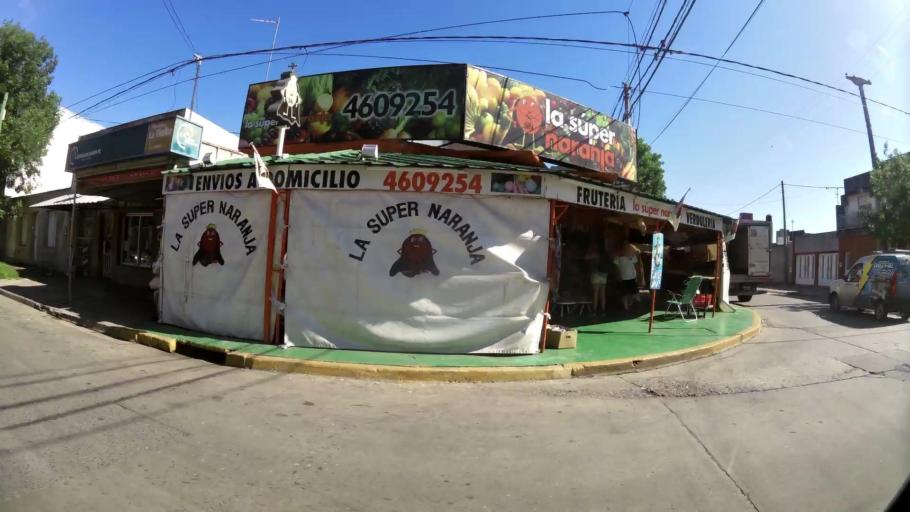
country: AR
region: Santa Fe
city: Santa Fe de la Vera Cruz
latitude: -31.6209
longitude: -60.6839
